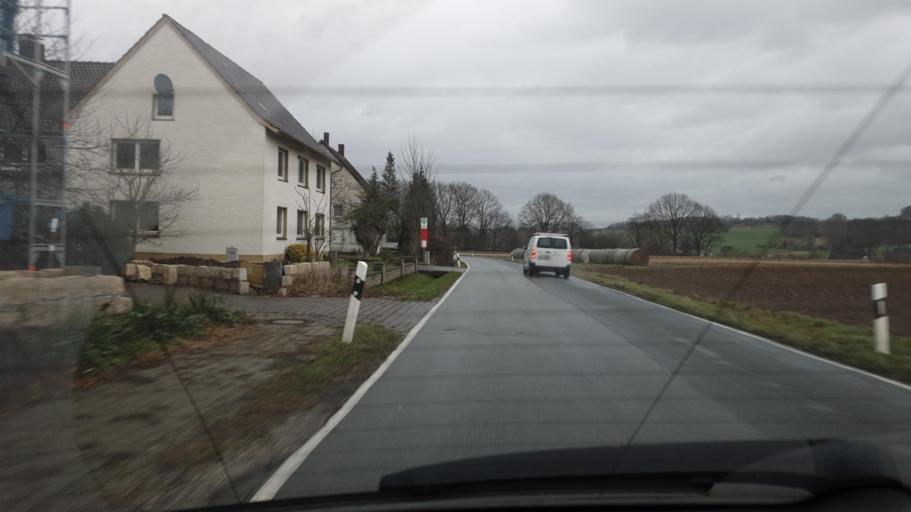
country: DE
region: North Rhine-Westphalia
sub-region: Regierungsbezirk Detmold
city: Detmold
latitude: 51.9721
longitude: 8.8409
